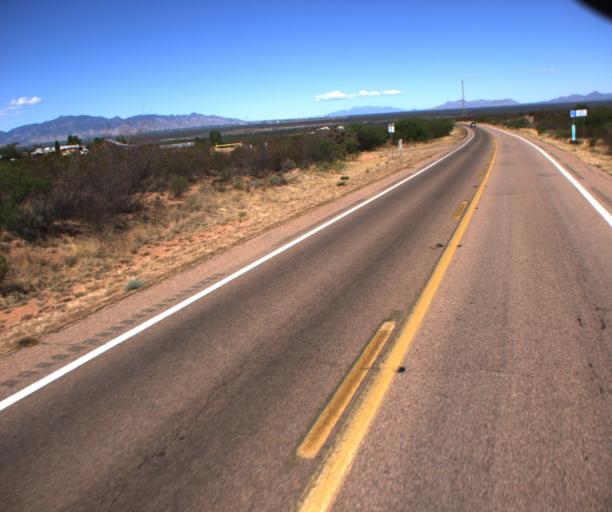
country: US
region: Arizona
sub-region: Cochise County
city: Sierra Vista Southeast
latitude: 31.5471
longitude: -110.0993
